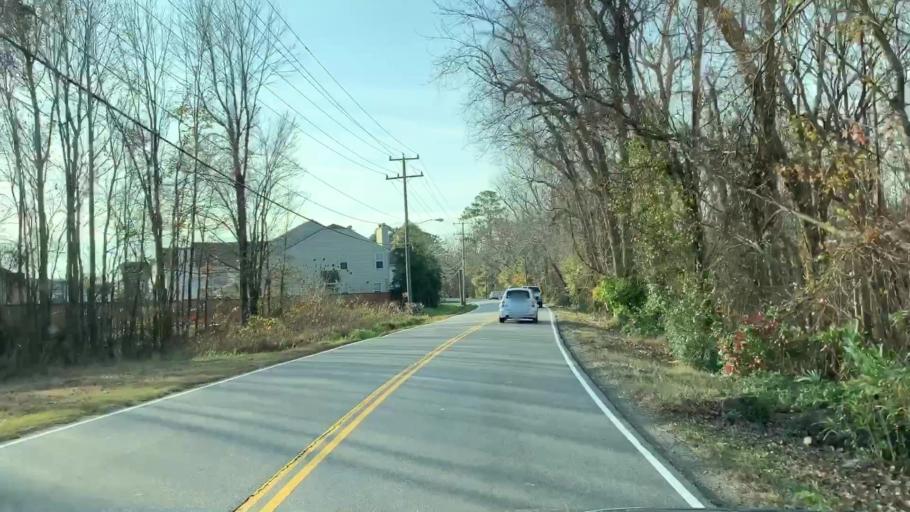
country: US
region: Virginia
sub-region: City of Chesapeake
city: Chesapeake
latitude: 36.7827
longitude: -76.1586
